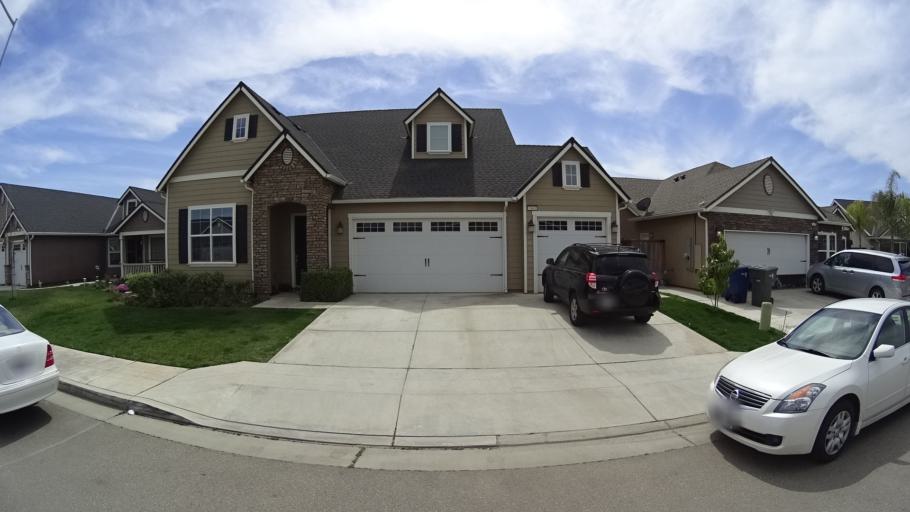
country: US
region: California
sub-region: Fresno County
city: Biola
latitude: 36.8117
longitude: -119.9240
